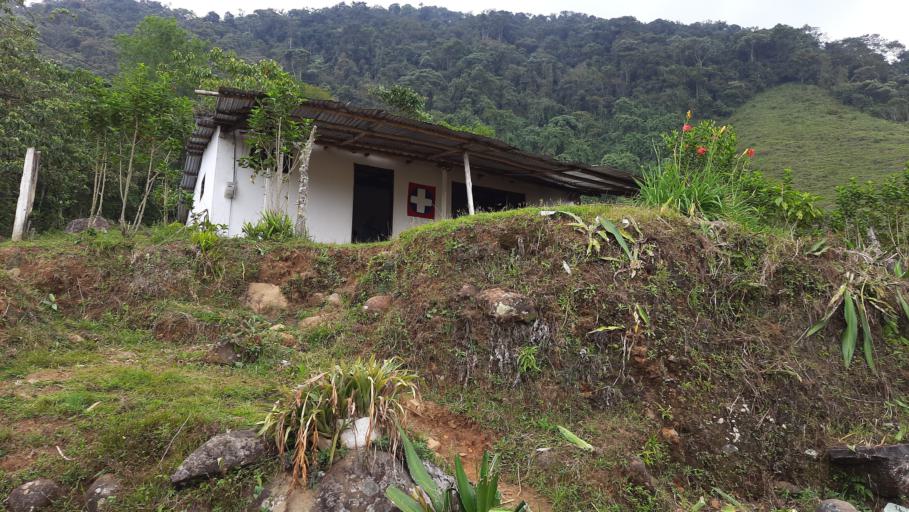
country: CO
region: Cauca
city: Buenos Aires
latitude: 3.1786
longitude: -76.7239
